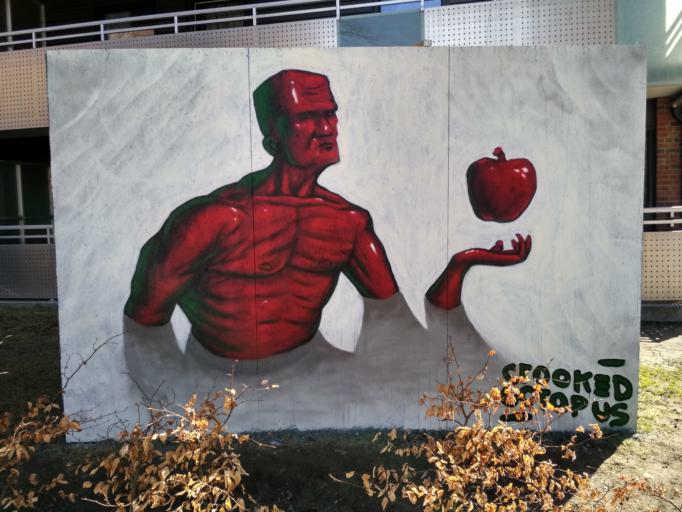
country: NO
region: Oslo
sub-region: Oslo
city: Oslo
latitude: 59.9139
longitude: 10.7731
